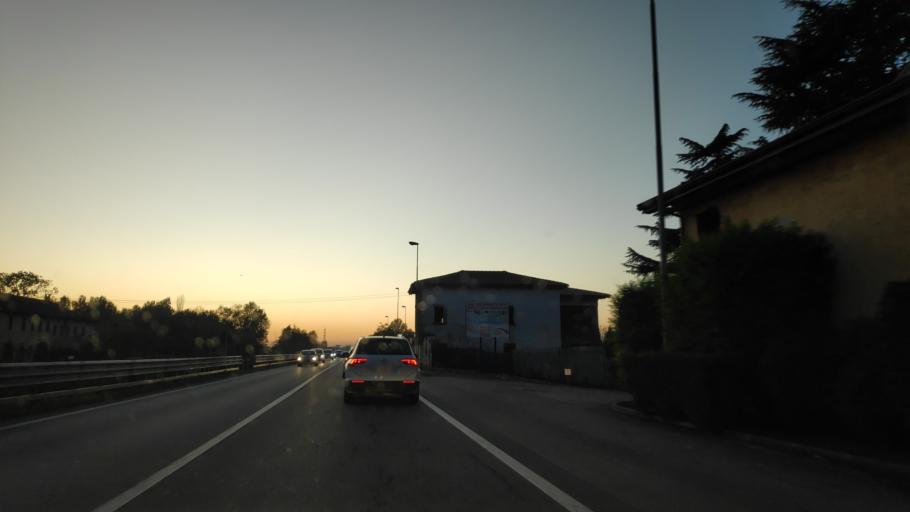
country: IT
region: Lombardy
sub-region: Citta metropolitana di Milano
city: Vermezzo
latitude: 45.4017
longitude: 8.9578
